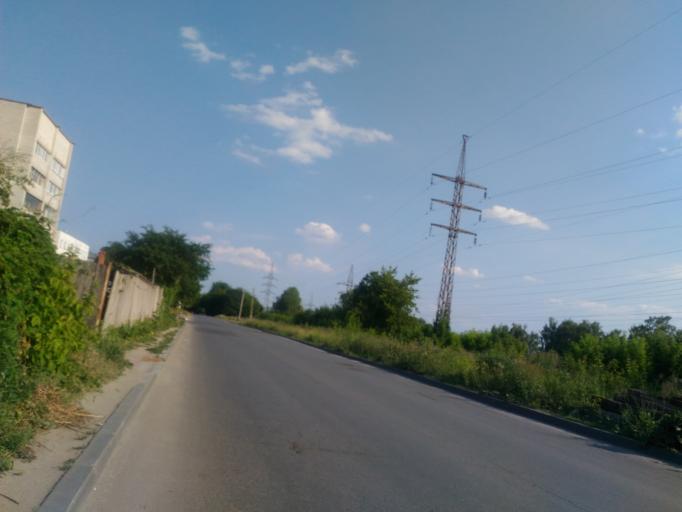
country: RU
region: Ulyanovsk
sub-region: Ulyanovskiy Rayon
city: Ulyanovsk
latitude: 54.3363
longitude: 48.3629
